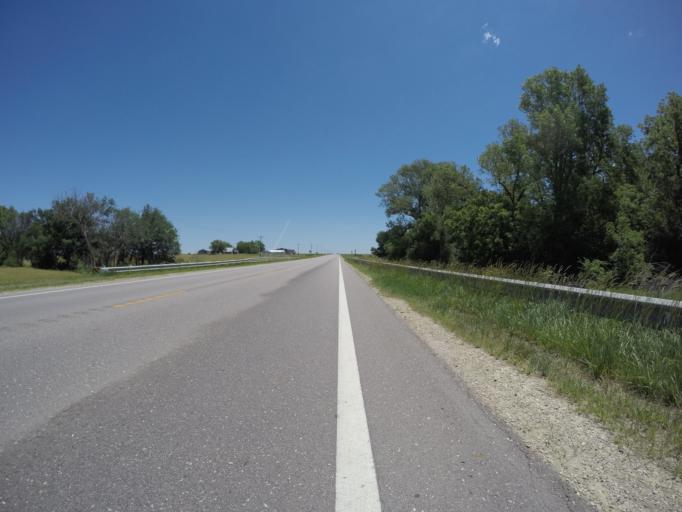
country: US
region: Kansas
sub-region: Republic County
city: Belleville
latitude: 39.8127
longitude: -97.6891
